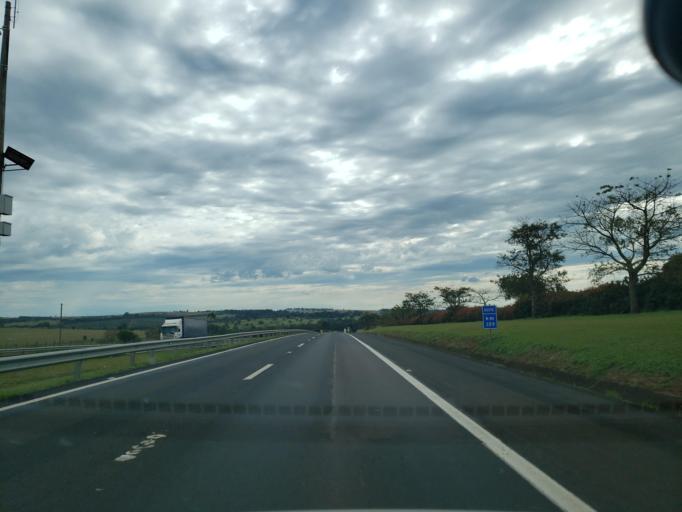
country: BR
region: Sao Paulo
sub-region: Bauru
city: Bauru
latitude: -22.2144
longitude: -49.1740
